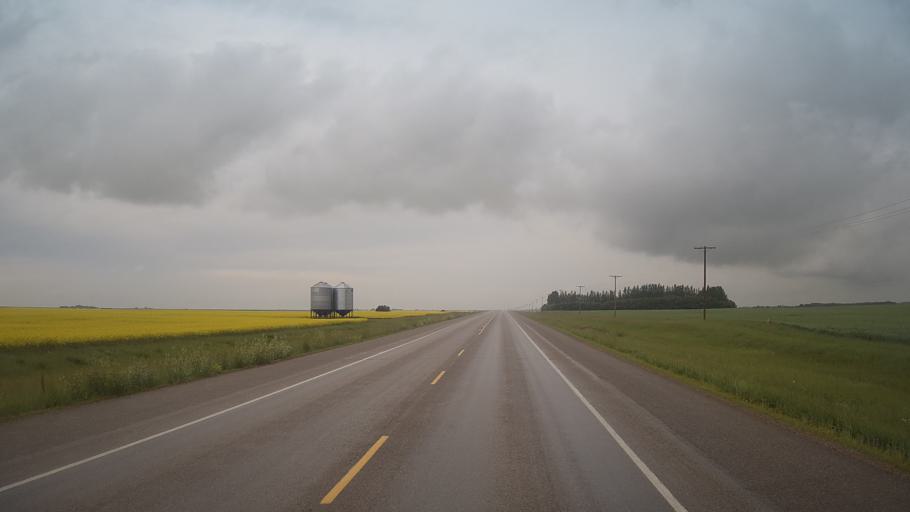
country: CA
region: Saskatchewan
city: Wilkie
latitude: 52.4056
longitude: -108.7885
